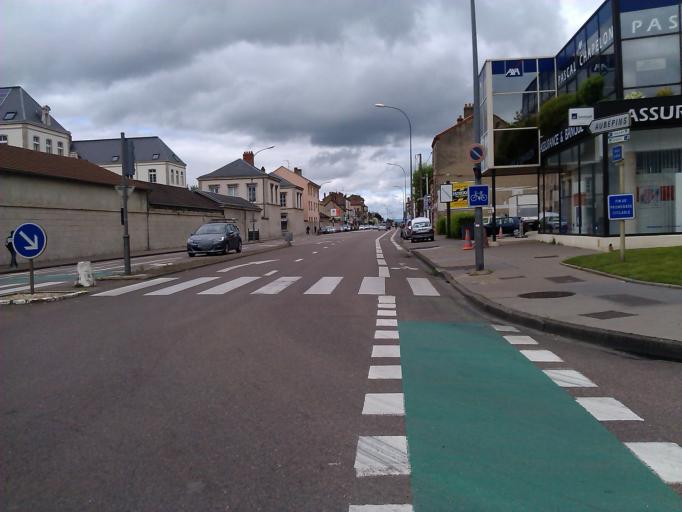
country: FR
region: Bourgogne
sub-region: Departement de Saone-et-Loire
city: Chalon-sur-Saone
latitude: 46.7918
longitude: 4.8497
